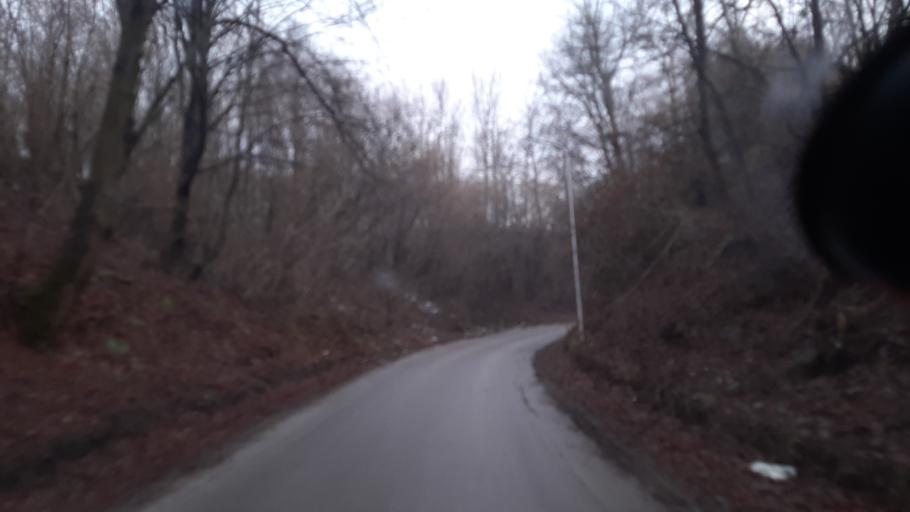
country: PL
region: Lublin Voivodeship
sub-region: Powiat lubelski
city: Lublin
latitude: 51.3160
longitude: 22.5782
